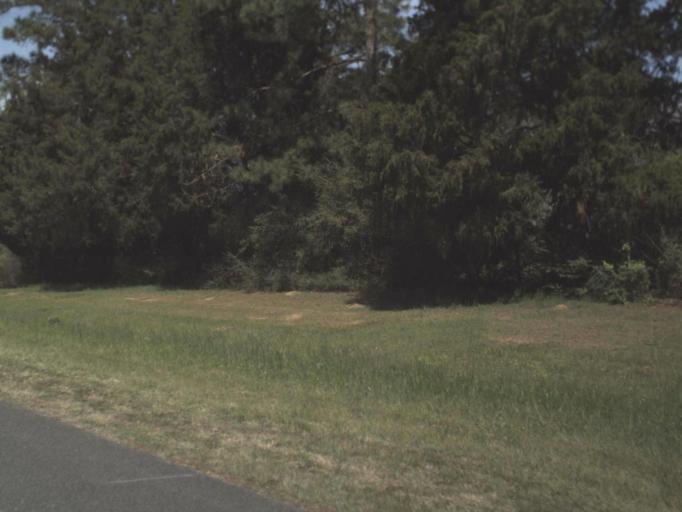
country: US
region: Florida
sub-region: Holmes County
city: Bonifay
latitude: 30.7927
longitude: -85.7147
